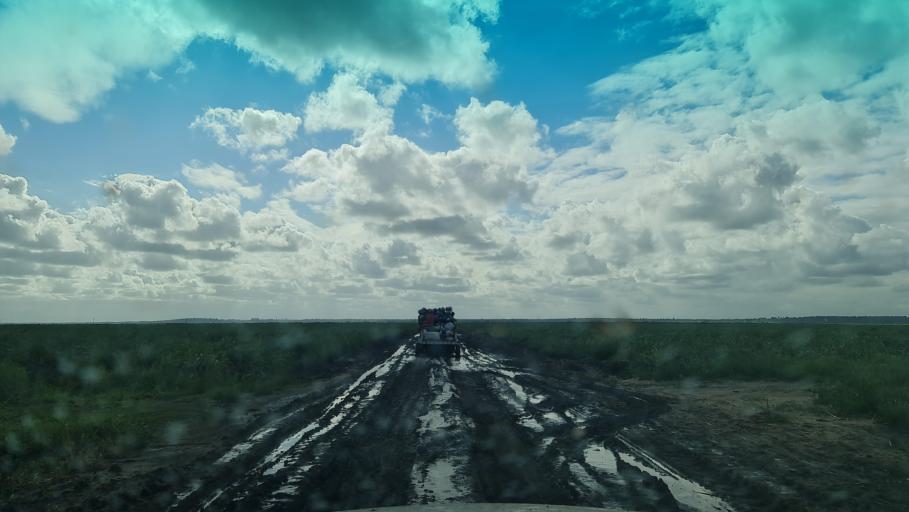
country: MZ
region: Maputo
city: Manhica
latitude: -25.4386
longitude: 32.8513
